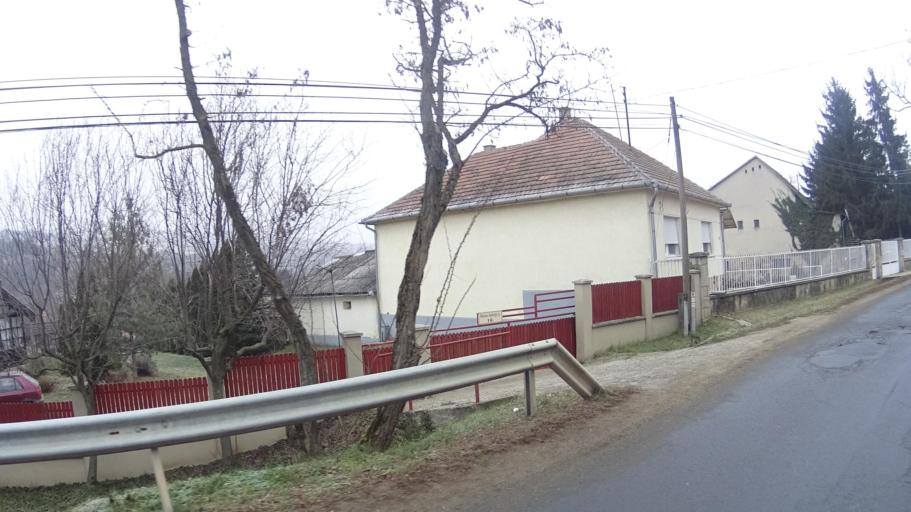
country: HU
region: Pest
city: Kosd
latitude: 47.8034
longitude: 19.1770
